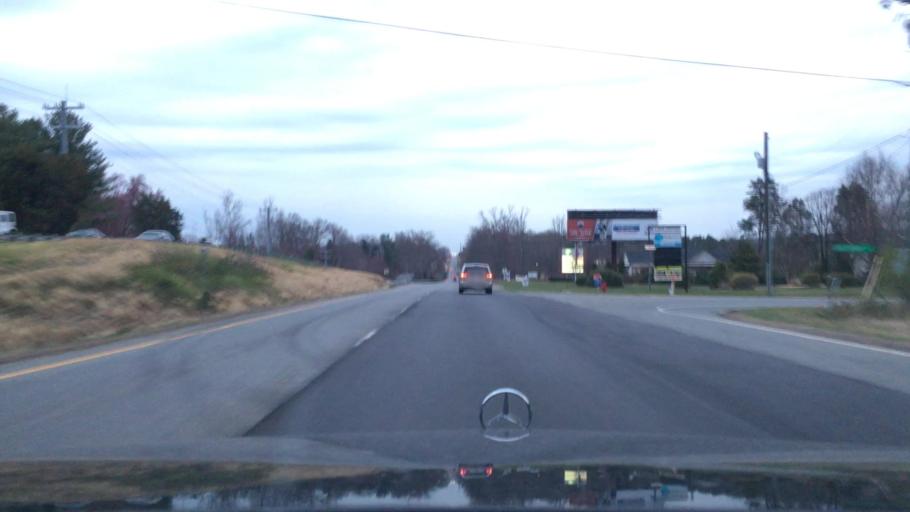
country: US
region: Virginia
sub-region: Greene County
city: Ruckersville
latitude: 38.1924
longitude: -78.3962
